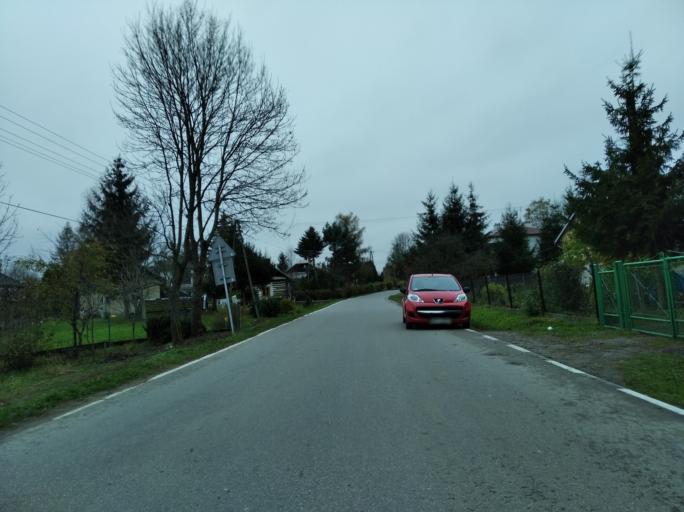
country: PL
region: Subcarpathian Voivodeship
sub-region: Powiat krosnienski
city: Leki
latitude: 49.8062
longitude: 21.6618
